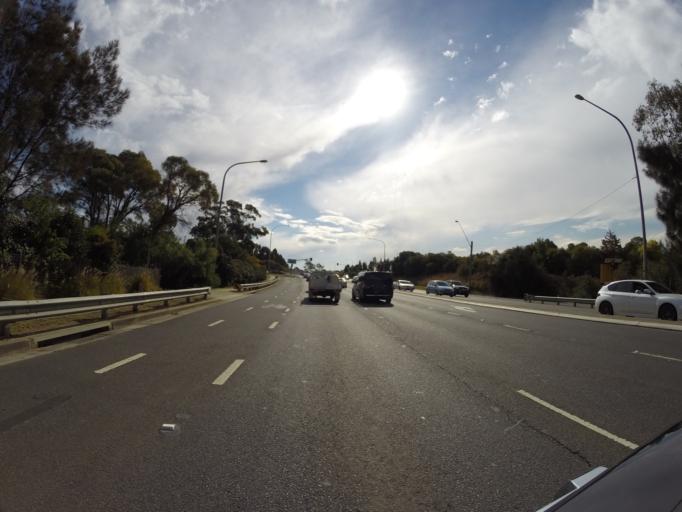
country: AU
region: New South Wales
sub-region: Campbelltown Municipality
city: Campbelltown
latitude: -34.0690
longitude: 150.8032
